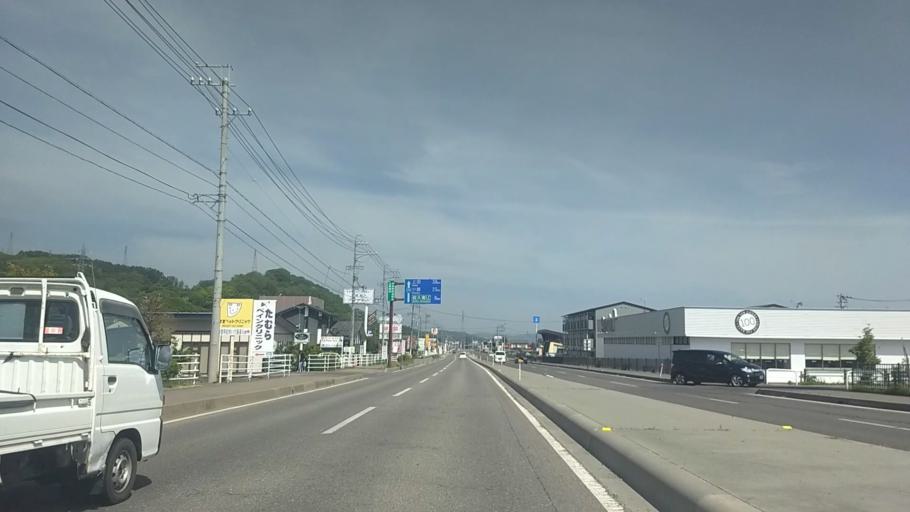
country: JP
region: Nagano
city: Saku
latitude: 36.1947
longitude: 138.4772
